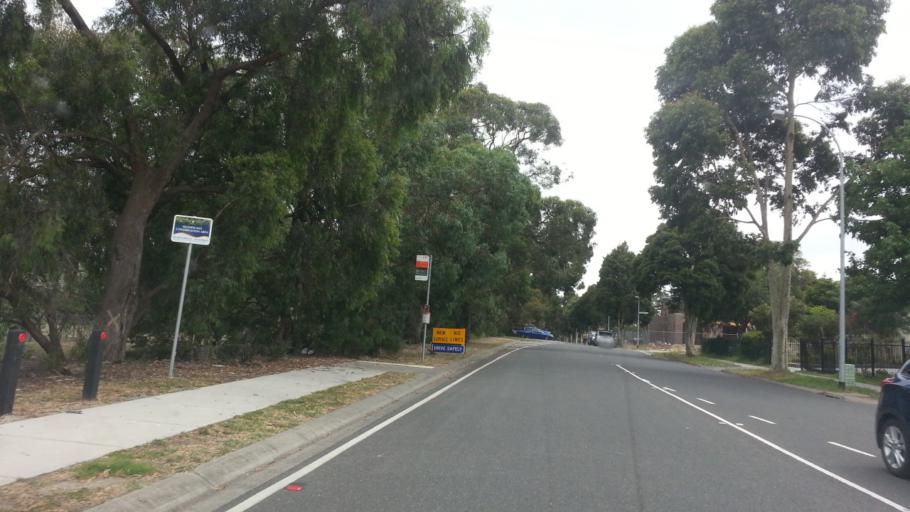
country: AU
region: Victoria
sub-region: Knox
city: Scoresby
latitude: -37.9114
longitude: 145.2471
